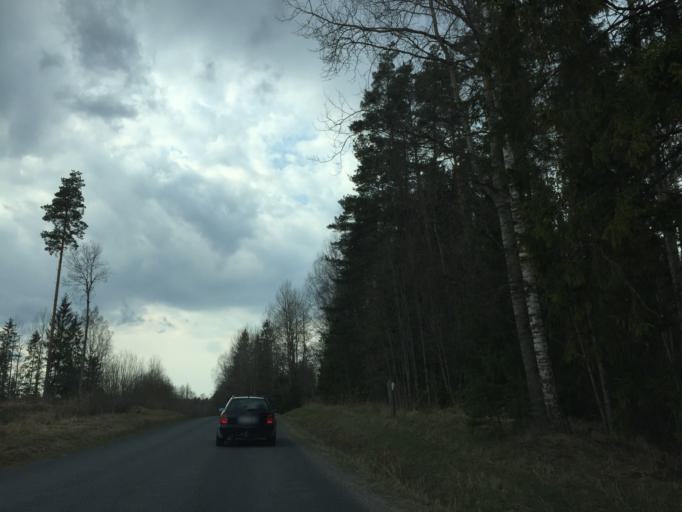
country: RU
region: Pskov
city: Pechory
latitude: 57.7377
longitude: 27.3195
